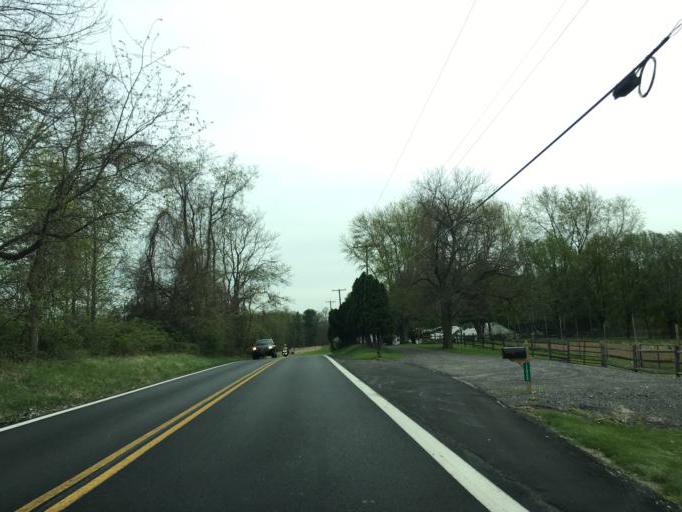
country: US
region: Maryland
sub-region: Baltimore County
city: Hampton
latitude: 39.4797
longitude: -76.5727
